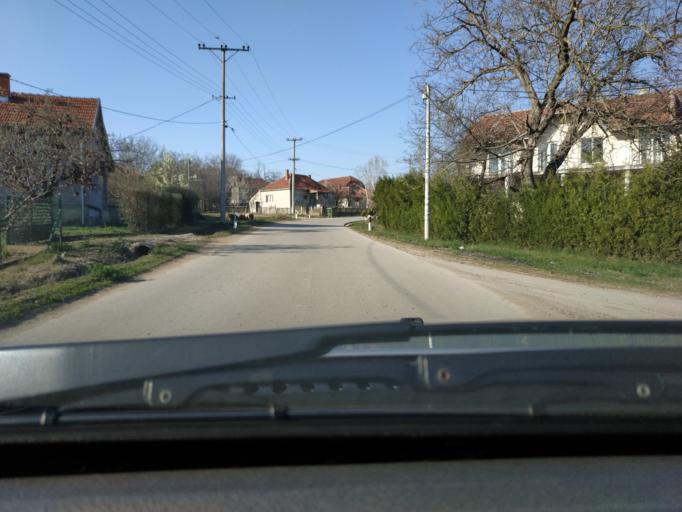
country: RS
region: Central Serbia
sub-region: Nisavski Okrug
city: Aleksinac
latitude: 43.4961
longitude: 21.7858
